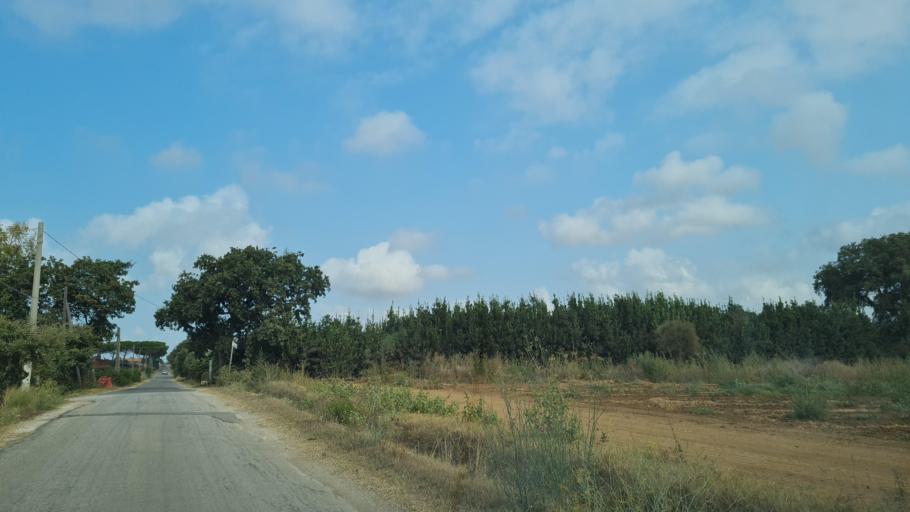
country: IT
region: Latium
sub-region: Provincia di Viterbo
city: Montalto di Castro
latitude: 42.3080
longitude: 11.6225
